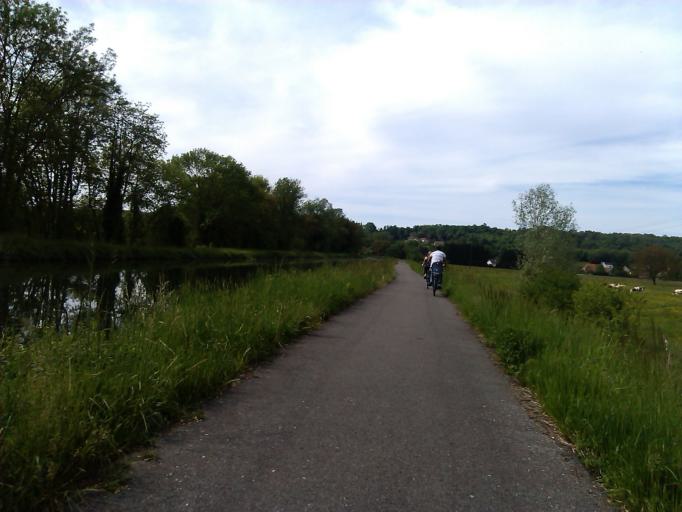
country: FR
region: Franche-Comte
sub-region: Departement du Doubs
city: Saint-Vit
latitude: 47.1594
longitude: 5.8548
